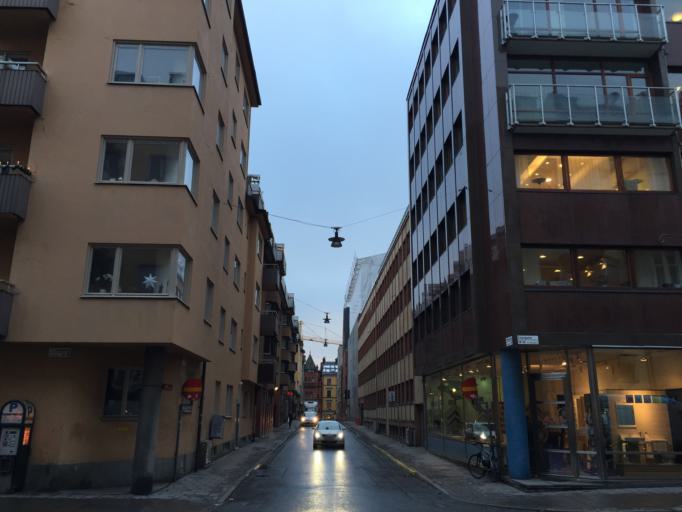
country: SE
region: Stockholm
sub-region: Stockholms Kommun
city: OEstermalm
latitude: 59.3377
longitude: 18.0785
